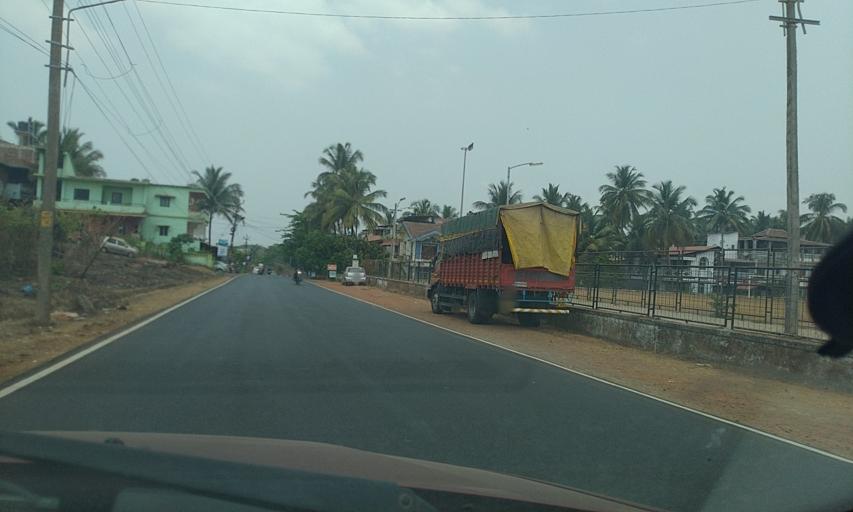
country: IN
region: Goa
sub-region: North Goa
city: Mapuca
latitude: 15.6058
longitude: 73.8035
